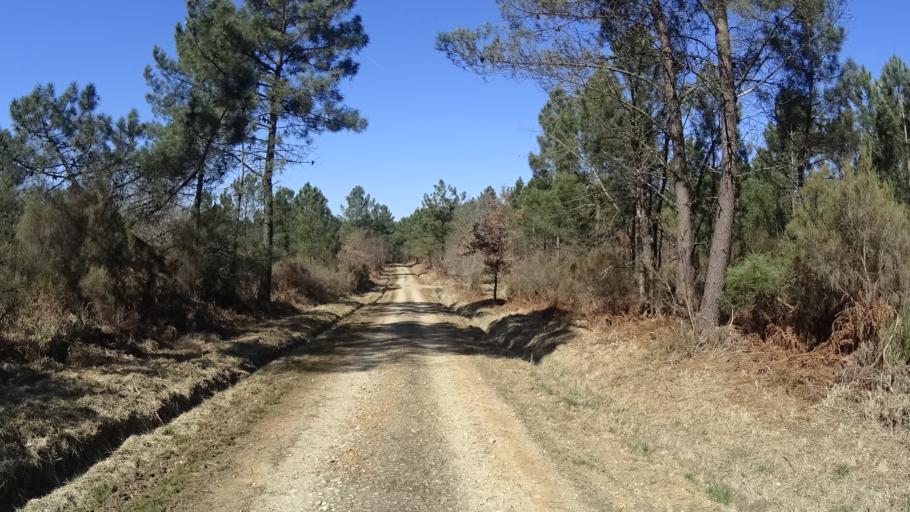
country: FR
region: Aquitaine
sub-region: Departement de la Dordogne
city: Riberac
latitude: 45.1879
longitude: 0.3112
